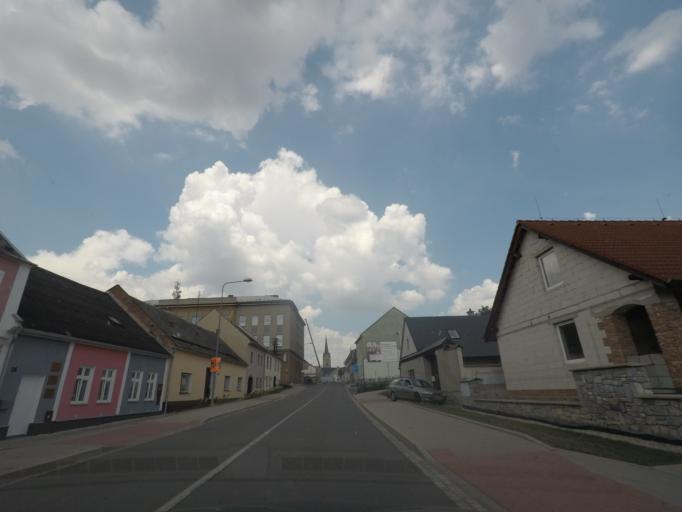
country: CZ
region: Olomoucky
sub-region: Okres Sumperk
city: Mohelnice
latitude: 49.7734
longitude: 16.9180
